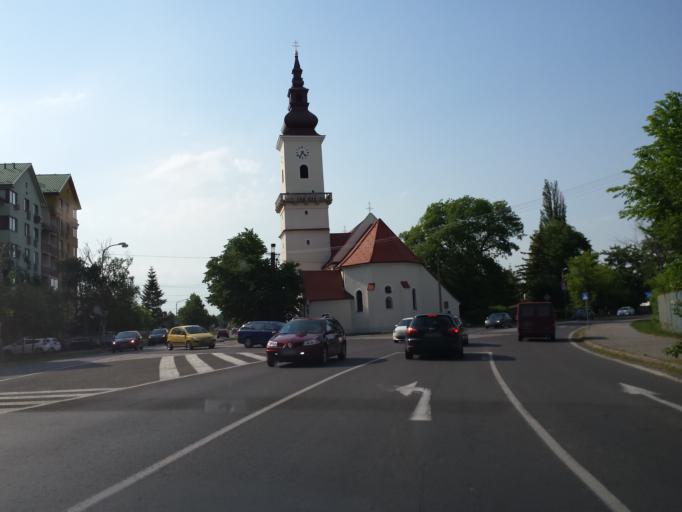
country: SK
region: Bratislavsky
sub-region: Okres Malacky
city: Malacky
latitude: 48.4400
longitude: 17.0128
